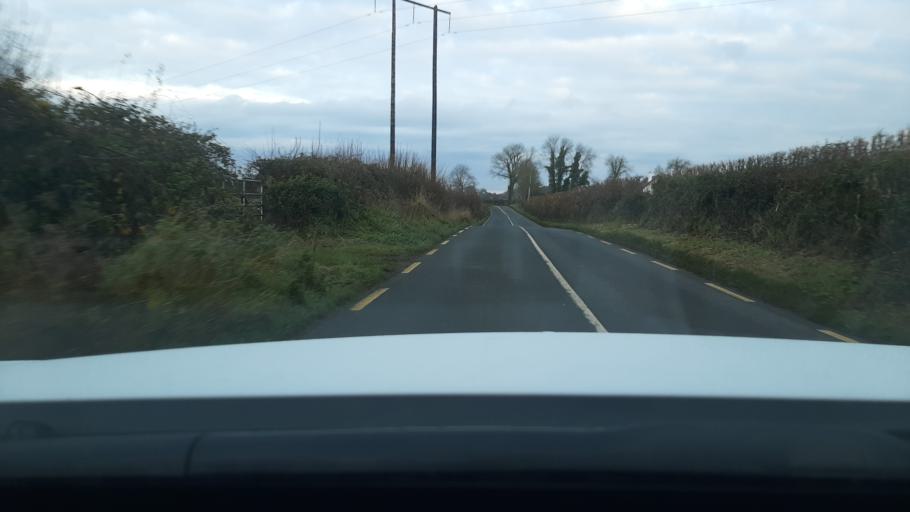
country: IE
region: Leinster
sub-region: Kildare
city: Rathangan
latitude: 53.2303
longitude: -7.0074
